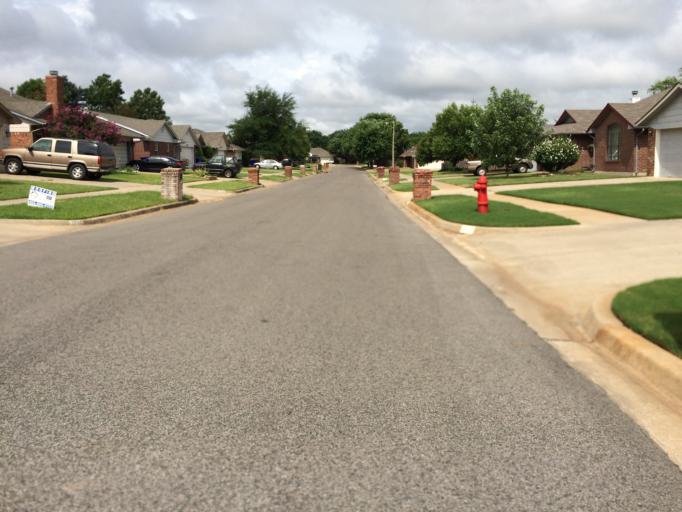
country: US
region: Oklahoma
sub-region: Cleveland County
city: Hall Park
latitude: 35.2229
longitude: -97.4142
